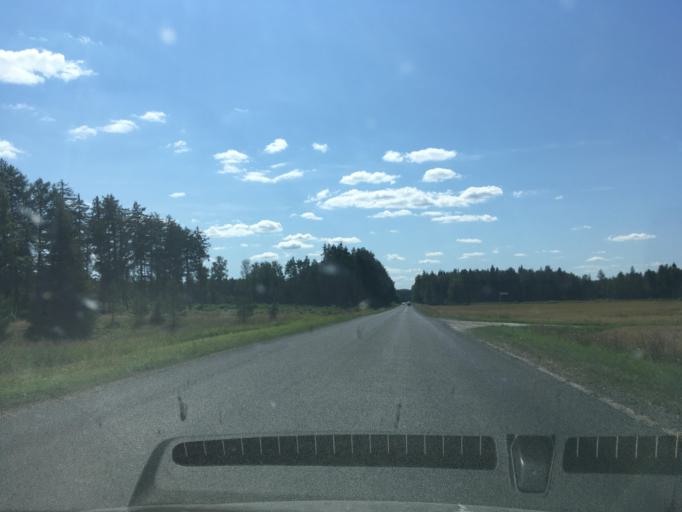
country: EE
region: Jogevamaa
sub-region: Jogeva linn
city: Jogeva
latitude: 58.7475
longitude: 26.3102
